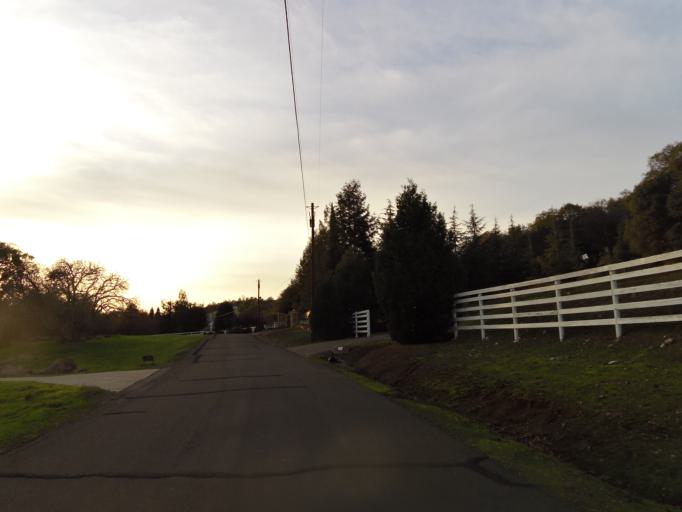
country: US
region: California
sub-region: El Dorado County
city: Cameron Park
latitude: 38.7444
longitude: -120.9936
